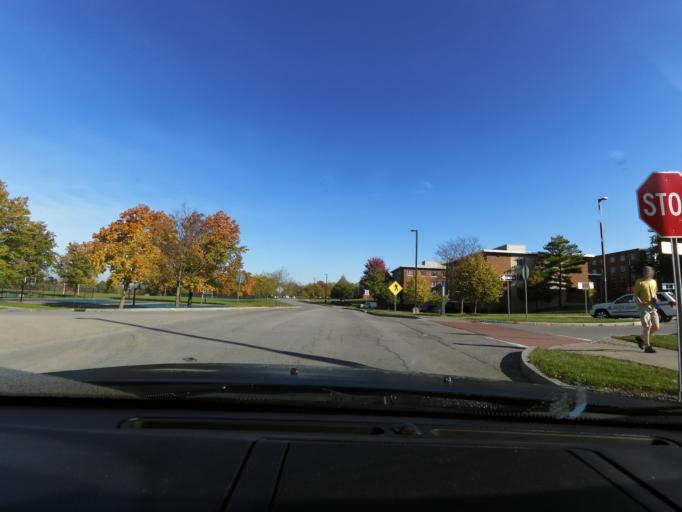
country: US
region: New York
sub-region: Livingston County
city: Geneseo
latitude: 42.7988
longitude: -77.8233
